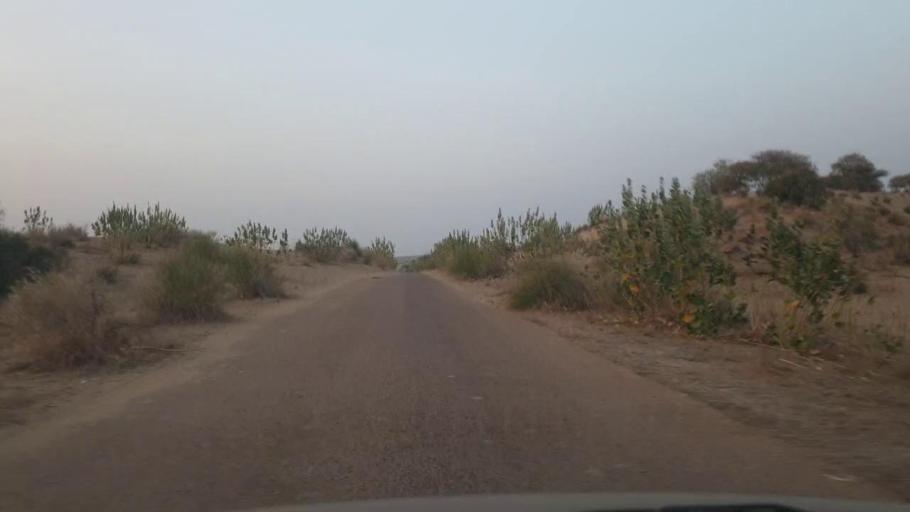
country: PK
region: Sindh
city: Umarkot
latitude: 25.3438
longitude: 70.0508
